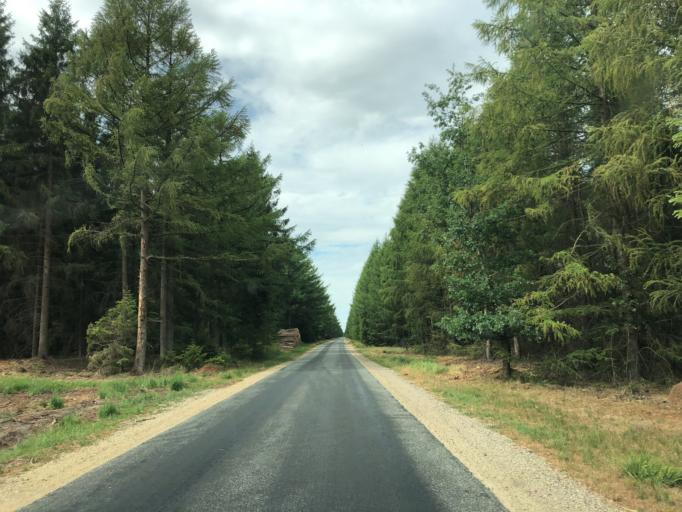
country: DK
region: South Denmark
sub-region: Billund Kommune
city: Grindsted
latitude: 55.6462
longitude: 8.9139
